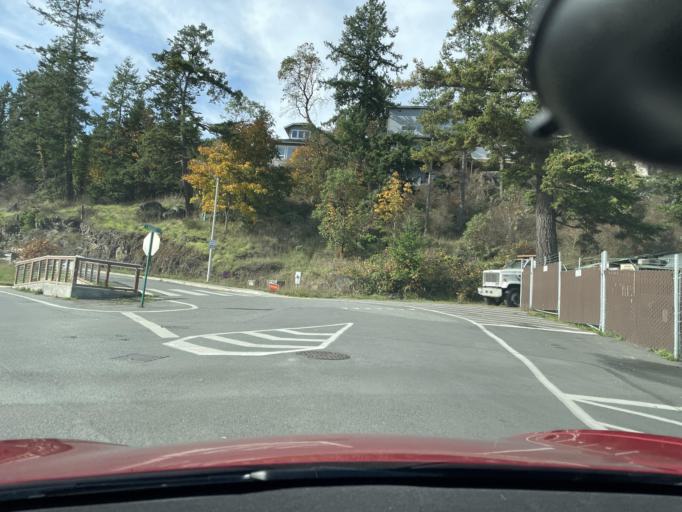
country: US
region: Washington
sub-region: San Juan County
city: Friday Harbor
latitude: 48.5312
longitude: -123.0270
